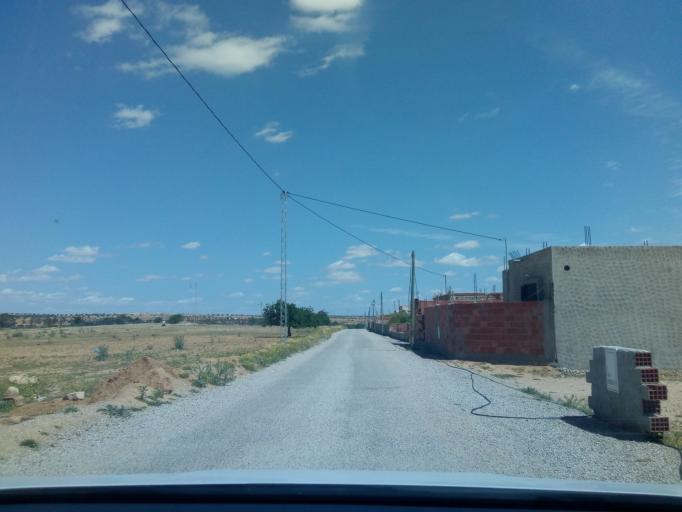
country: TN
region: Safaqis
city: Sfax
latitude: 34.7328
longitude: 10.4921
